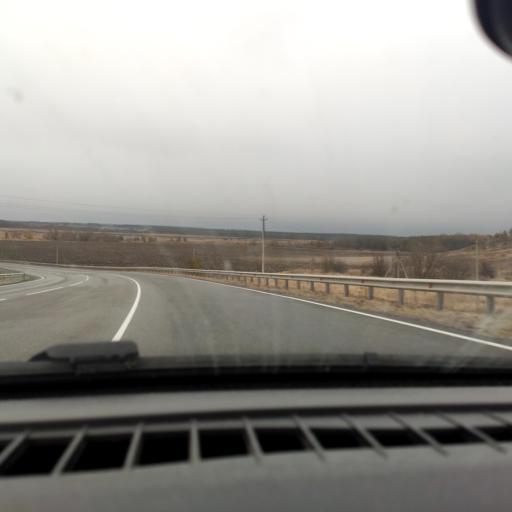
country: RU
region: Voronezj
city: Ostrogozhsk
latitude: 51.0258
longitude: 38.9867
